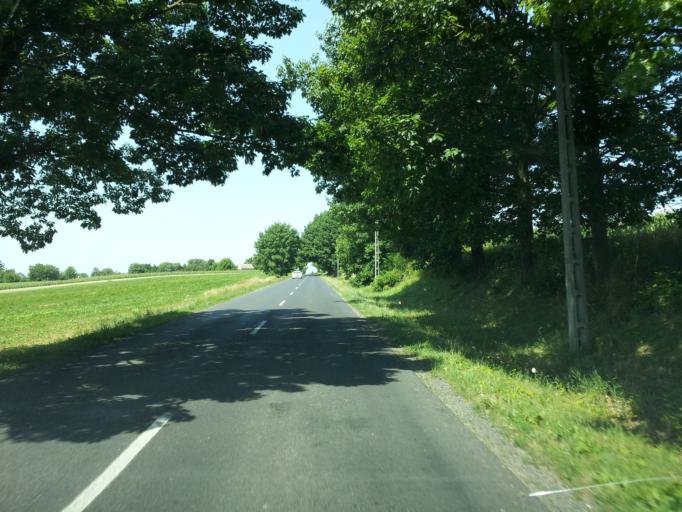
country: HU
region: Zala
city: Zalaegerszeg
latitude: 46.8602
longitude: 16.8134
